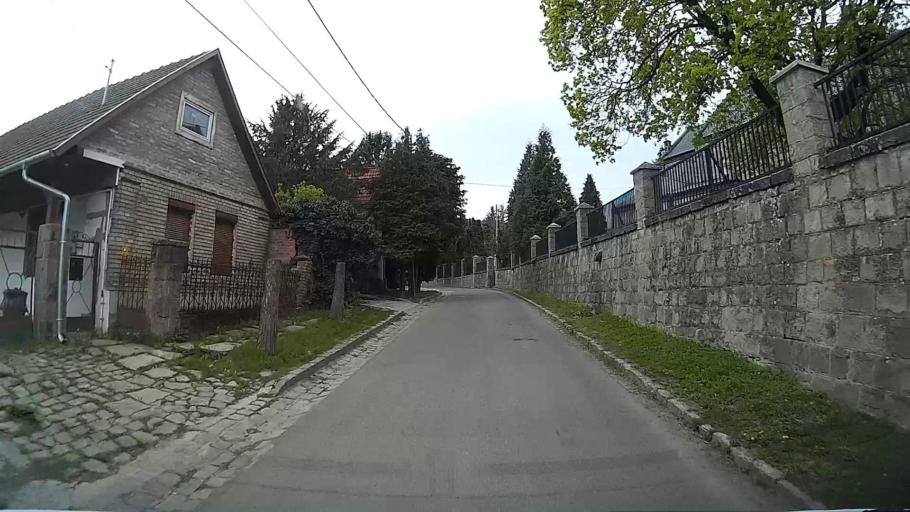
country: HU
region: Pest
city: Dunabogdany
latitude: 47.7915
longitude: 19.0333
